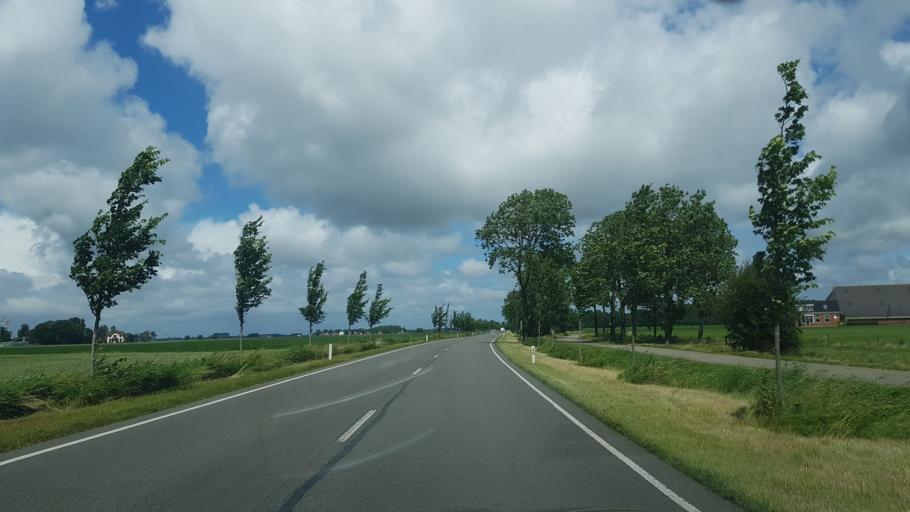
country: NL
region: Groningen
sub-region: Gemeente Winsum
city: Winsum
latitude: 53.3518
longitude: 6.5069
